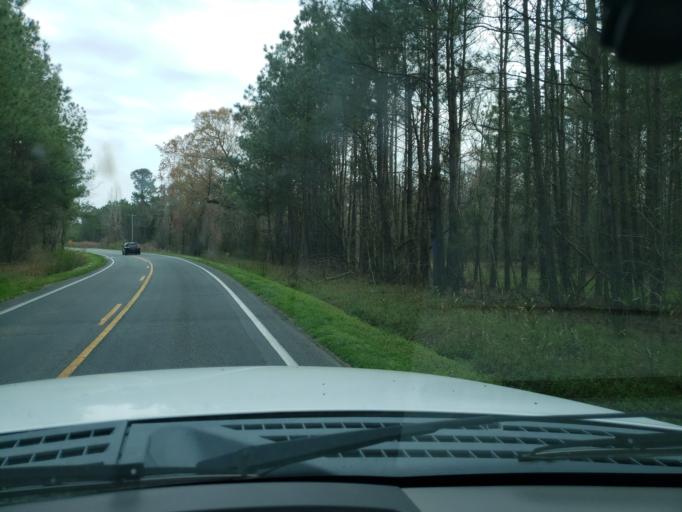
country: US
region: North Carolina
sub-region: Duplin County
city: Wallace
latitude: 34.7918
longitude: -77.8578
